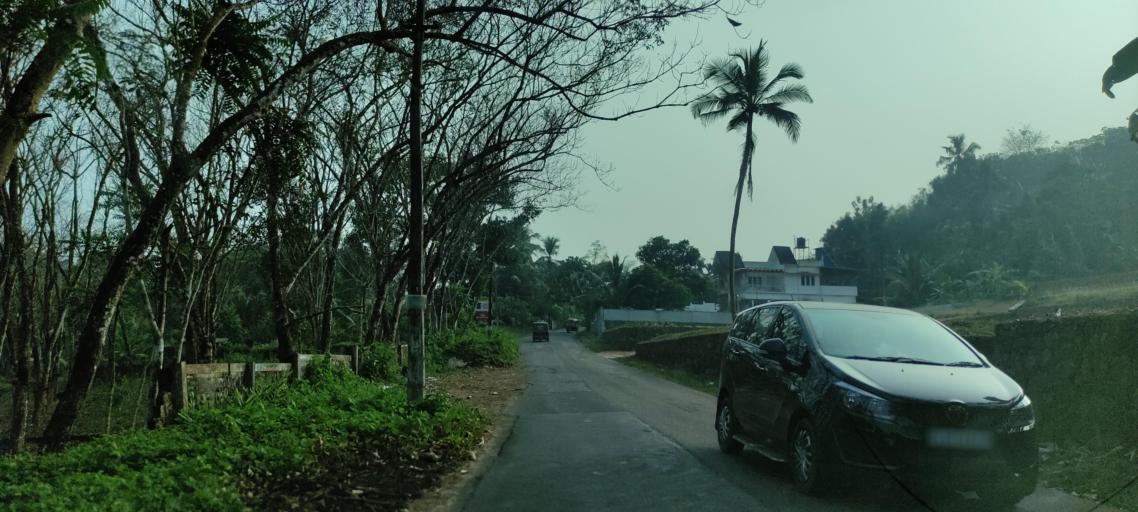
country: IN
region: Kerala
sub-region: Ernakulam
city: Piravam
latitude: 9.7923
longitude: 76.4996
